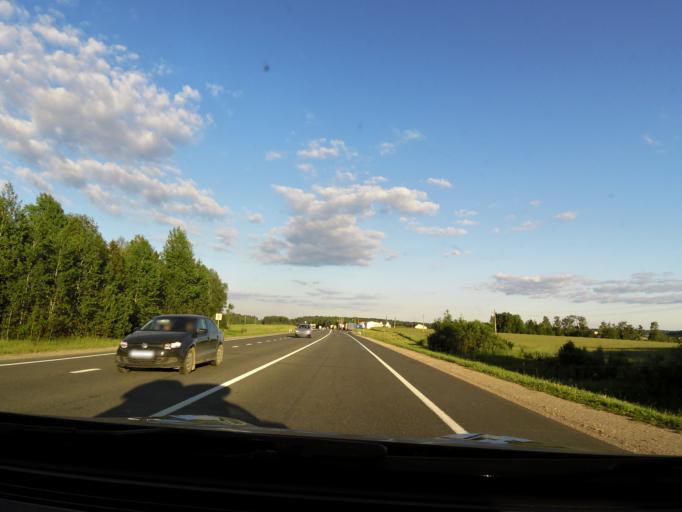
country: RU
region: Vologda
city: Vologda
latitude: 59.0751
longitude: 40.0220
